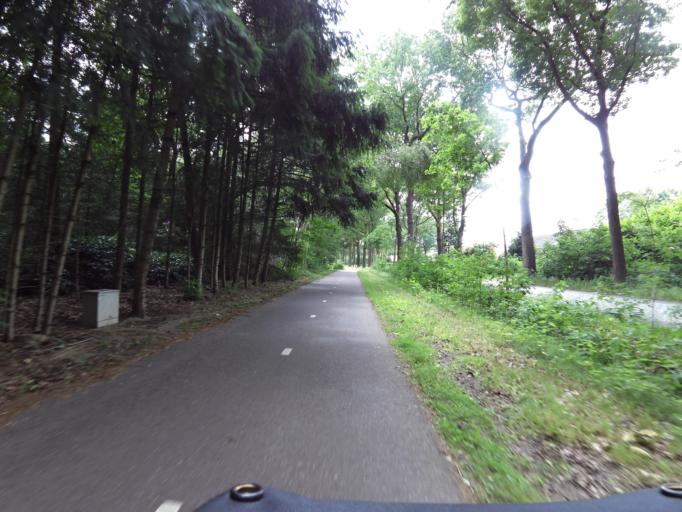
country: NL
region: North Brabant
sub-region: Gemeente Bladel en Netersel
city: Bladel
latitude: 51.3911
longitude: 5.2097
